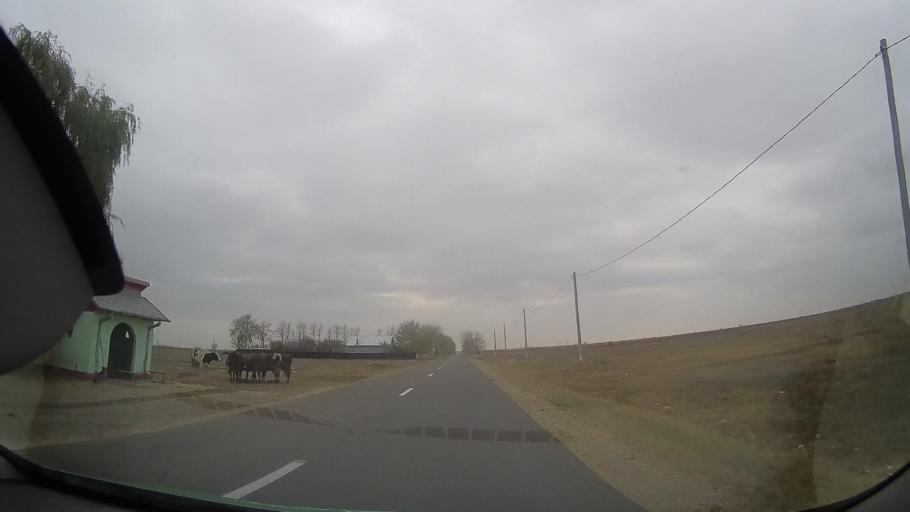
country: RO
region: Ialomita
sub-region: Comuna Garbovi
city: Garbovi
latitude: 44.7781
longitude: 26.7521
